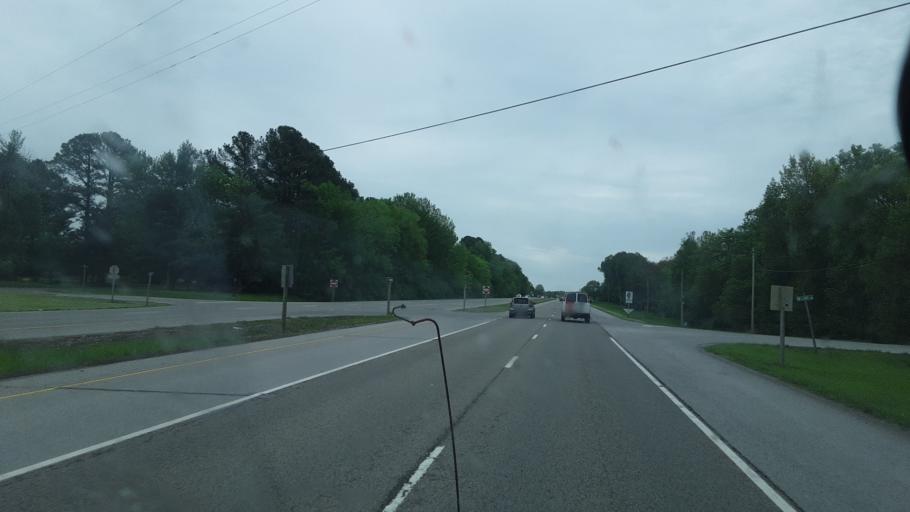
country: US
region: Illinois
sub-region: Jackson County
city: Carbondale
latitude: 37.7457
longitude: -89.2594
